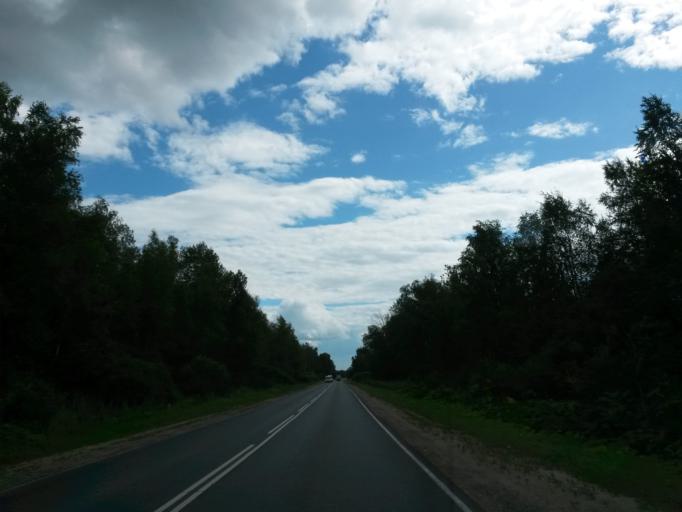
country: RU
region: Ivanovo
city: Pistsovo
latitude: 57.0741
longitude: 40.6847
